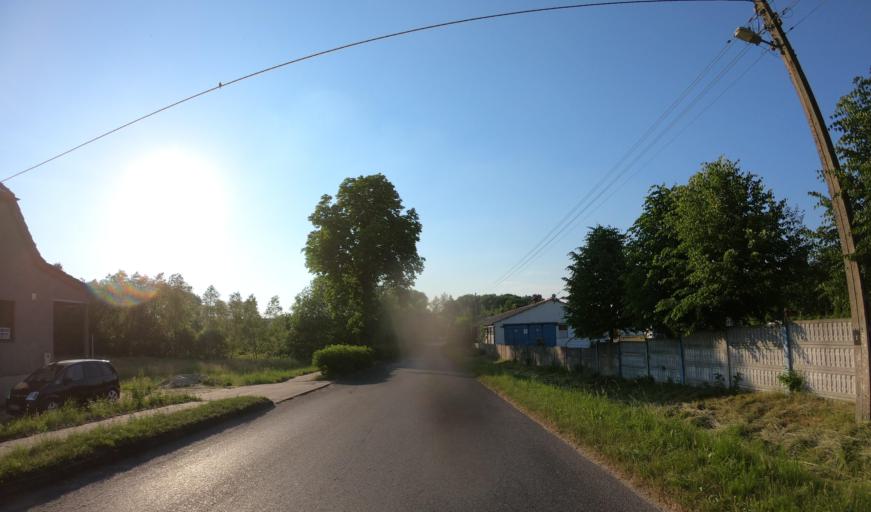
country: PL
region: West Pomeranian Voivodeship
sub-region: Powiat lobeski
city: Resko
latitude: 53.7650
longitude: 15.4052
